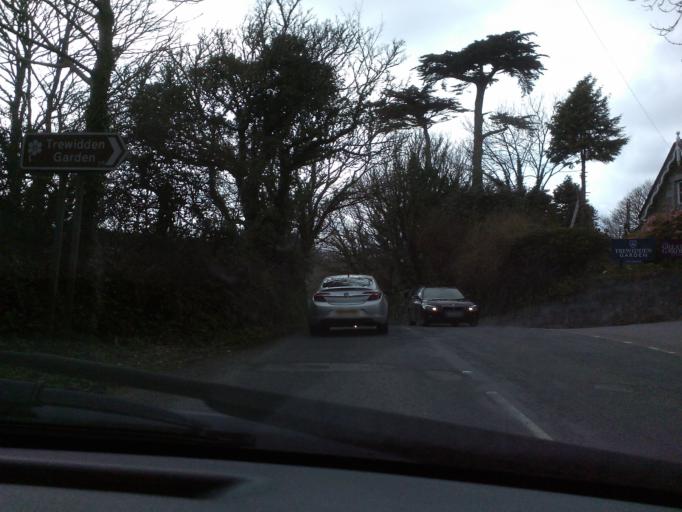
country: GB
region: England
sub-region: Cornwall
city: Penzance
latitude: 50.1076
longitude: -5.5692
